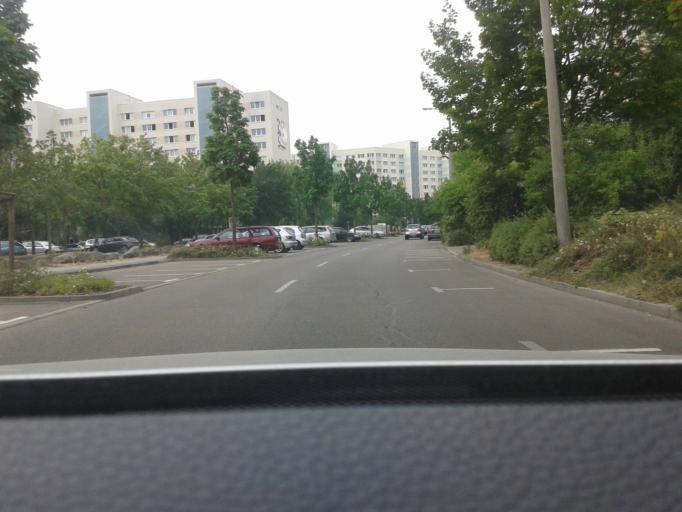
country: DE
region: Saxony
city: Dresden
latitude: 51.0083
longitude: 13.7972
